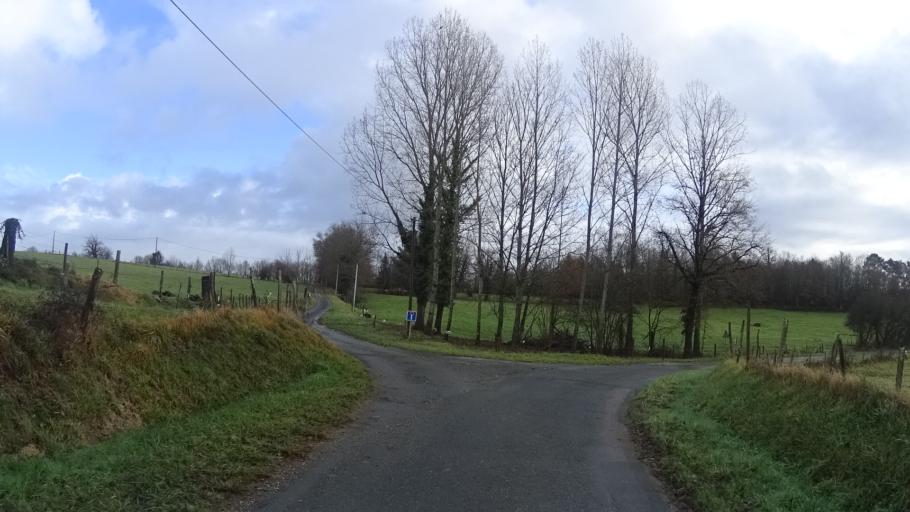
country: FR
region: Aquitaine
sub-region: Departement de la Dordogne
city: Thiviers
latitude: 45.4111
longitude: 0.9676
